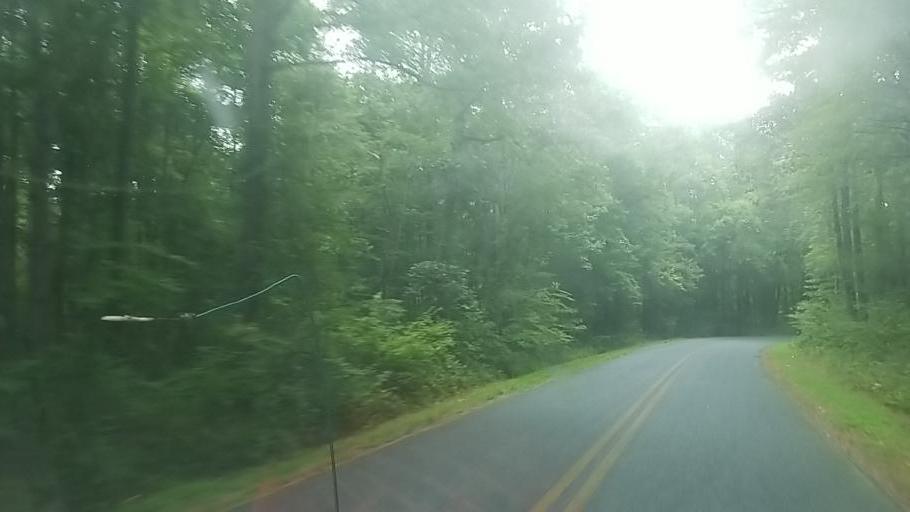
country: US
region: Maryland
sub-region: Wicomico County
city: Pittsville
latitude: 38.4151
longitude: -75.4805
